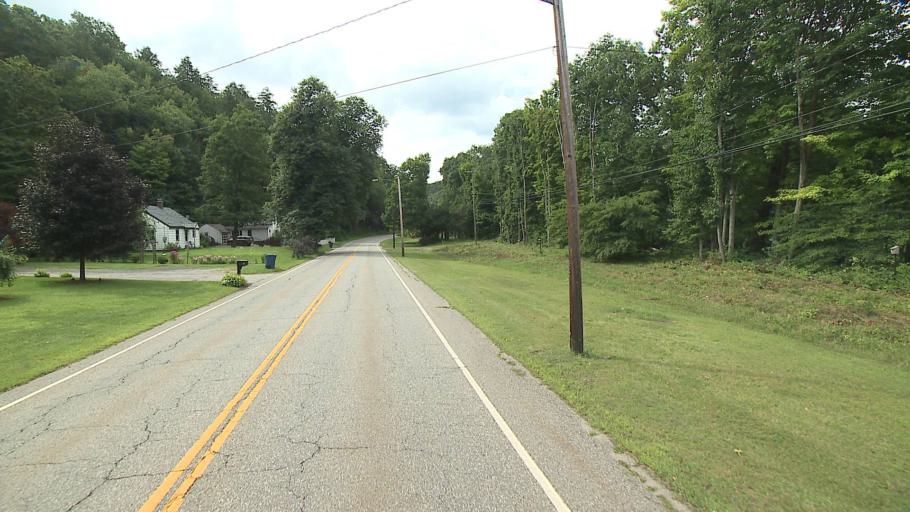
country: US
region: Connecticut
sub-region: Litchfield County
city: New Preston
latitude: 41.6484
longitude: -73.3171
